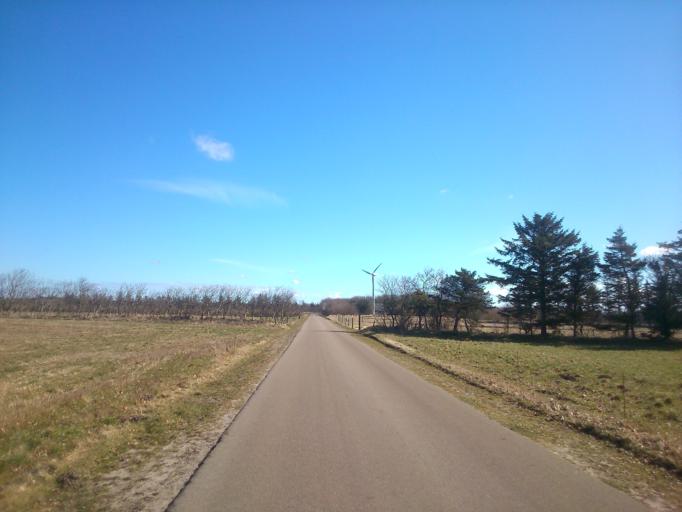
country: DK
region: Central Jutland
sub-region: Ringkobing-Skjern Kommune
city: Skjern
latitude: 55.9645
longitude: 8.4042
